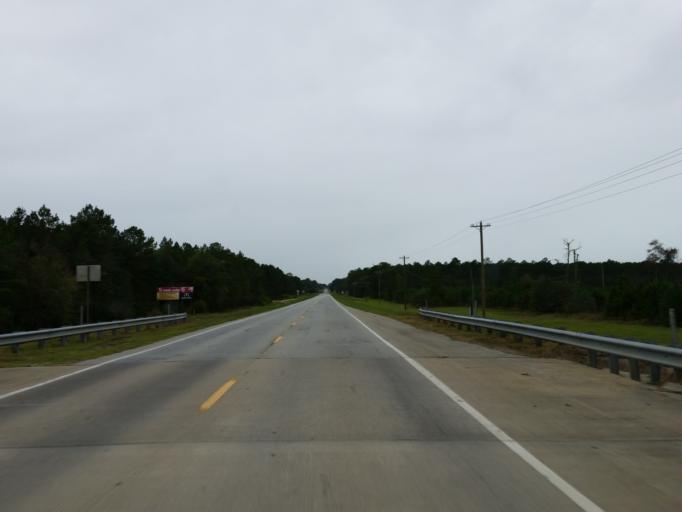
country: US
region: Georgia
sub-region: Lanier County
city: Lakeland
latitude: 31.0462
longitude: -83.0436
